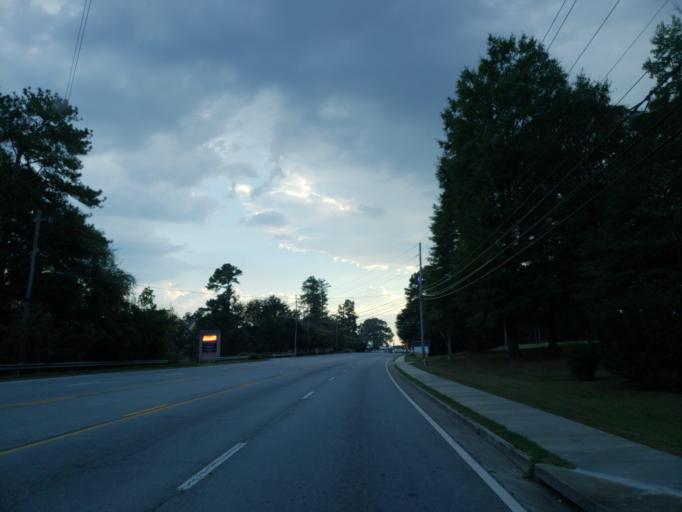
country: US
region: Georgia
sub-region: Cobb County
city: Powder Springs
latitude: 33.8725
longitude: -84.6256
